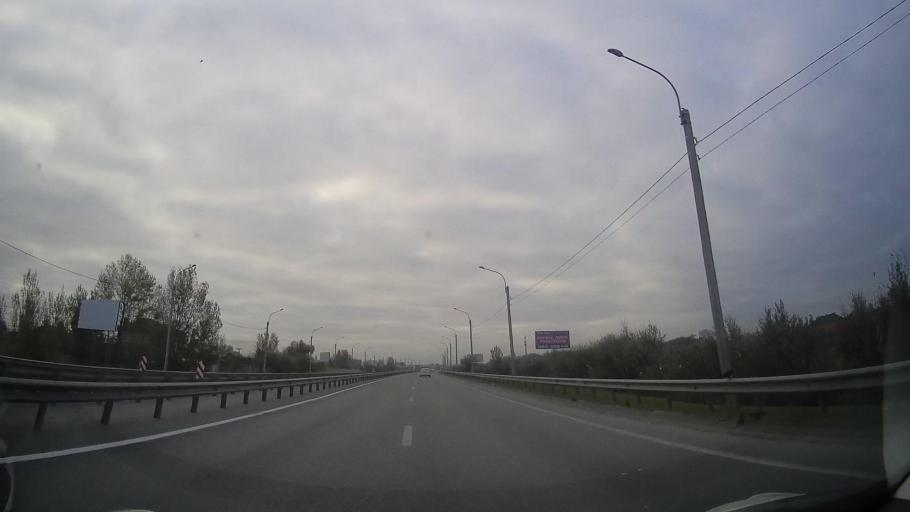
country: RU
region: Rostov
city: Bataysk
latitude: 47.1502
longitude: 39.7729
